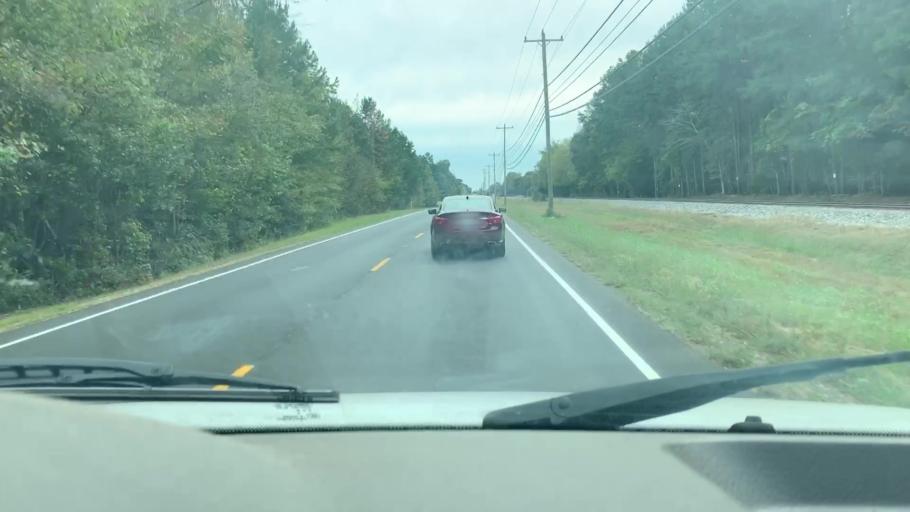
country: US
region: North Carolina
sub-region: Gaston County
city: Davidson
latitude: 35.5278
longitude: -80.8441
